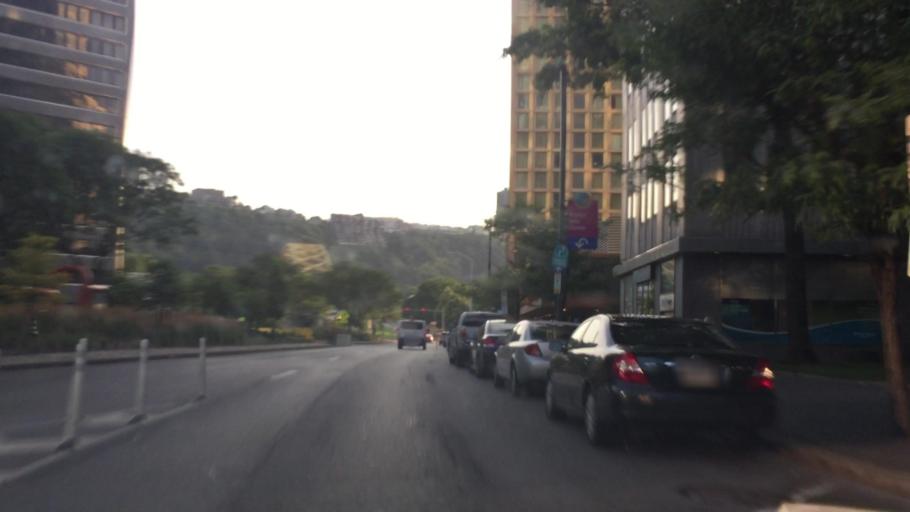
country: US
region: Pennsylvania
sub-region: Allegheny County
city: Pittsburgh
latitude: 40.4416
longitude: -80.0048
